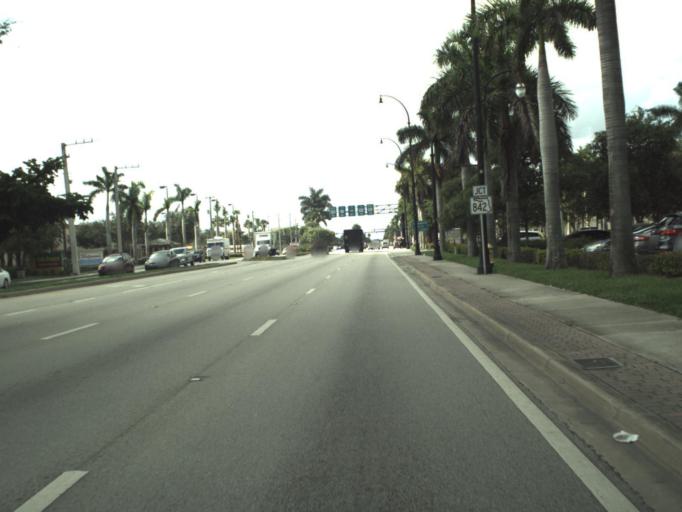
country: US
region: Florida
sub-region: Broward County
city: Broward Estates
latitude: 26.1245
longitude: -80.2022
